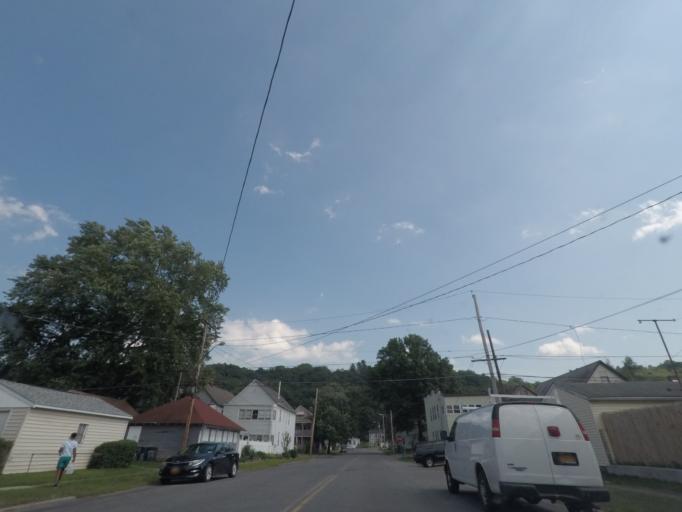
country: US
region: New York
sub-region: Saratoga County
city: Waterford
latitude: 42.7695
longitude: -73.6728
